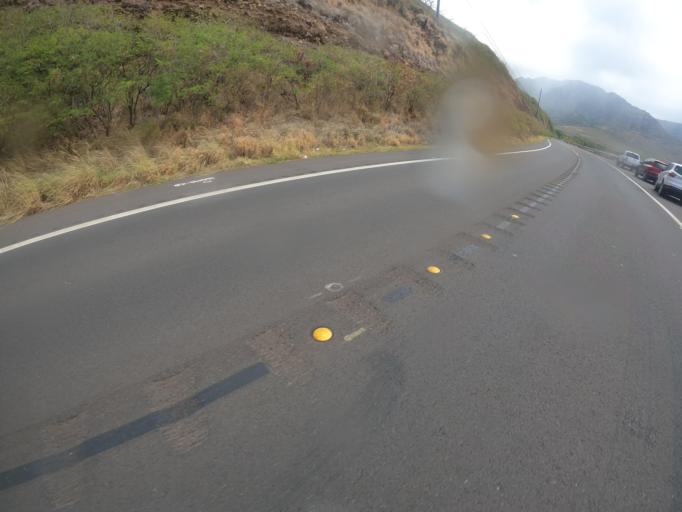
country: US
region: Hawaii
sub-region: Honolulu County
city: Makaha Valley
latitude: 21.5416
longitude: -158.2363
